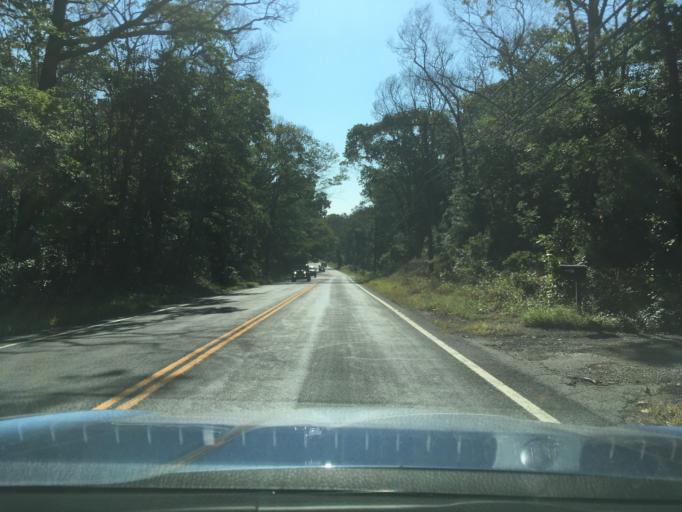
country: US
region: Rhode Island
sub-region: Washington County
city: Exeter
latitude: 41.5795
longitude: -71.5514
